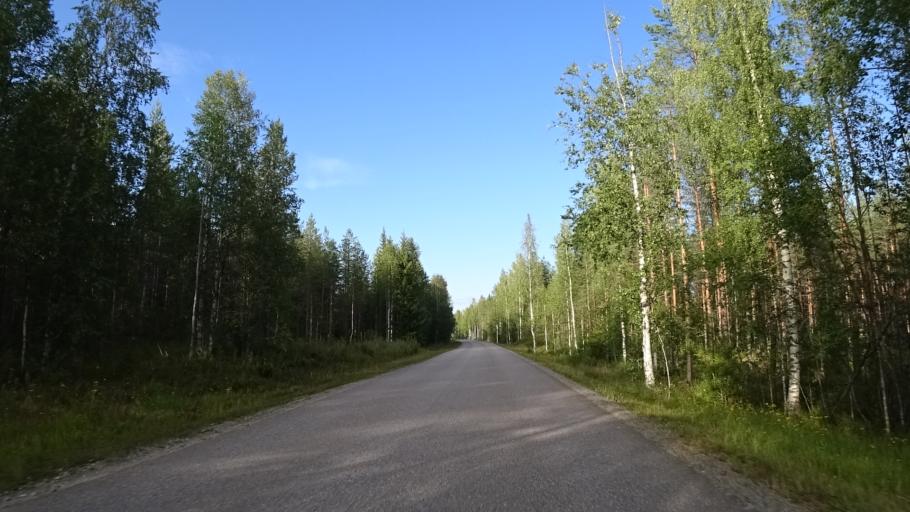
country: FI
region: North Karelia
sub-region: Joensuu
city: Eno
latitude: 63.0146
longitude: 30.4864
